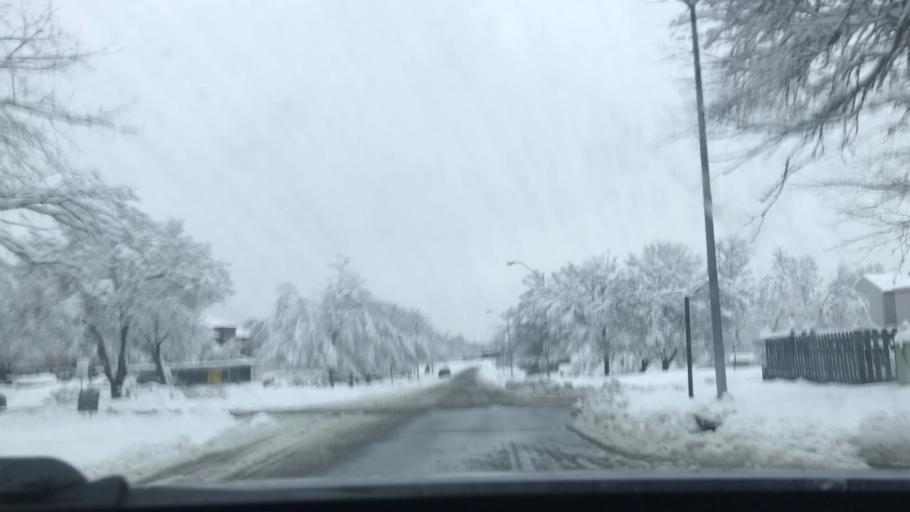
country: US
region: Missouri
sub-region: Jackson County
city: Grandview
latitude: 38.9182
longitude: -94.5301
